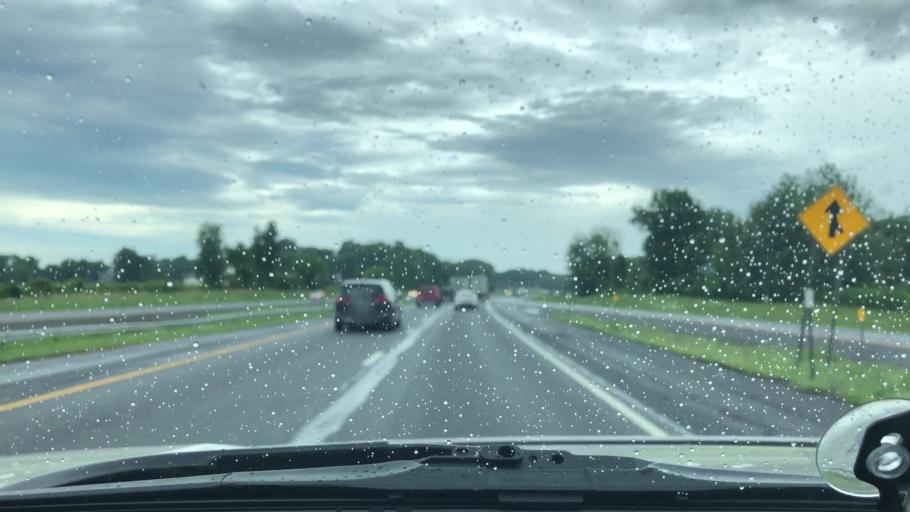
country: US
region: New York
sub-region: Rensselaer County
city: Castleton-on-Hudson
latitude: 42.5368
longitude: -73.7832
